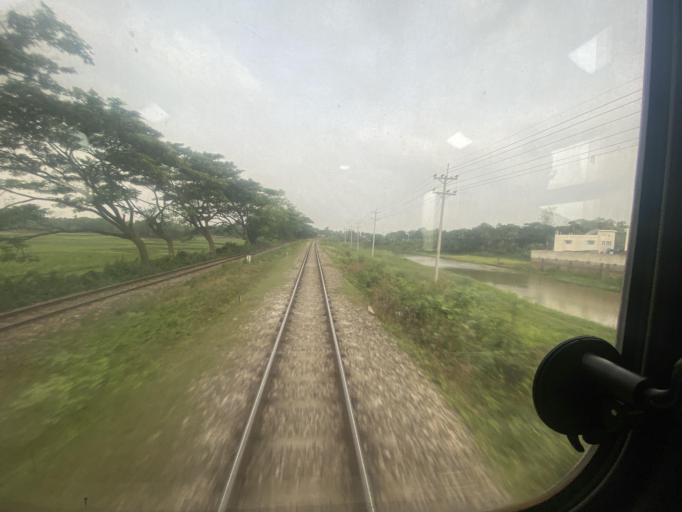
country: BD
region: Dhaka
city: Tungi
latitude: 23.9335
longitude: 90.4974
